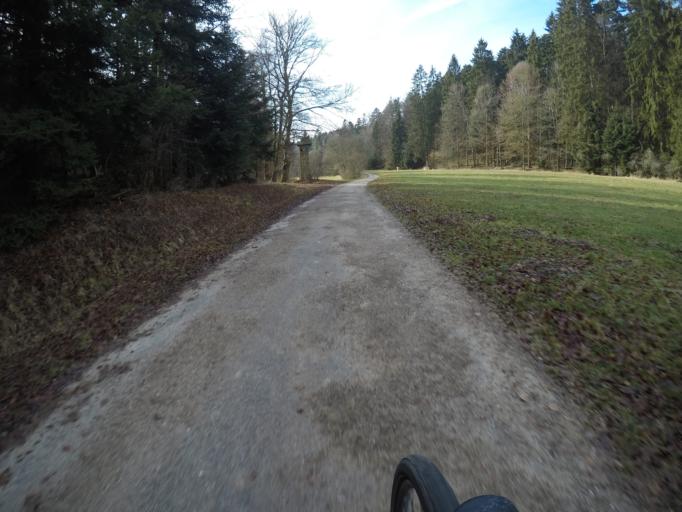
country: DE
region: Baden-Wuerttemberg
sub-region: Regierungsbezirk Stuttgart
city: Deckenpfronn
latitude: 48.6691
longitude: 8.7740
